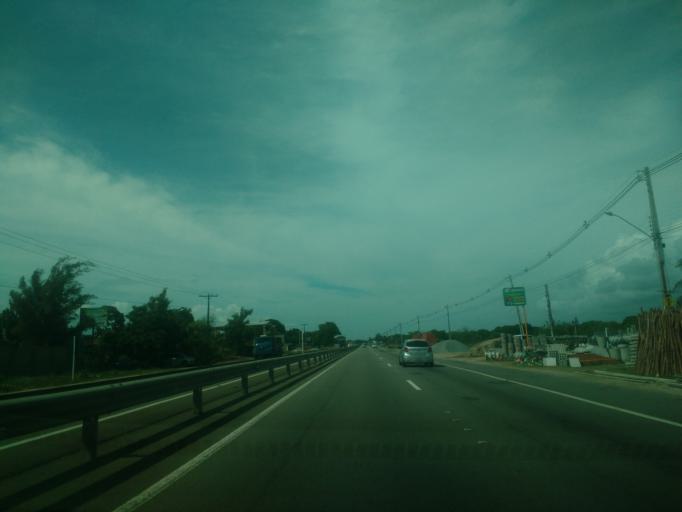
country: BR
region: Alagoas
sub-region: Marechal Deodoro
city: Marechal Deodoro
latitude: -9.7496
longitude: -35.8396
